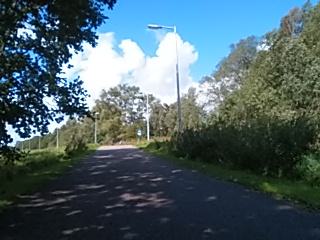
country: NL
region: North Holland
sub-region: Gemeente Diemen
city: Diemen
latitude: 52.3575
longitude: 4.9561
